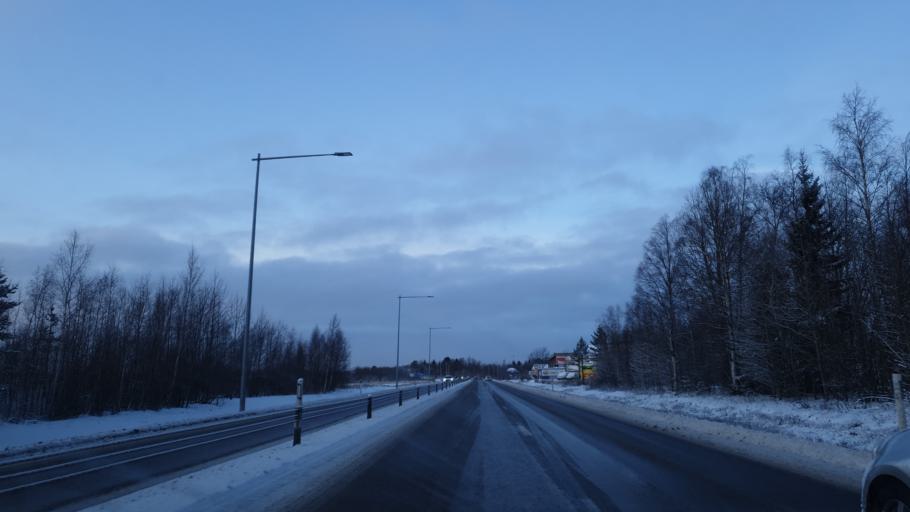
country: SE
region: Vaesterbotten
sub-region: Umea Kommun
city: Umea
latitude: 63.8009
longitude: 20.2718
